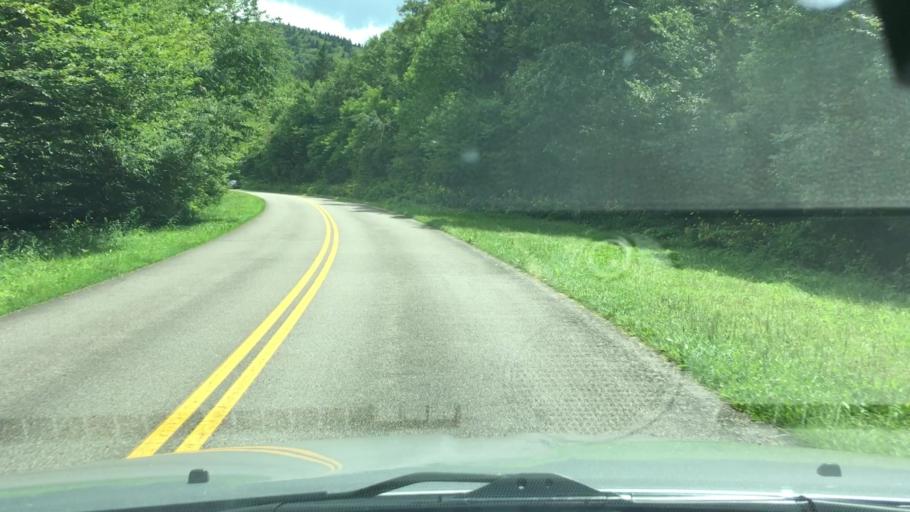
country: US
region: North Carolina
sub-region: Buncombe County
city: Black Mountain
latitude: 35.7134
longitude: -82.2748
